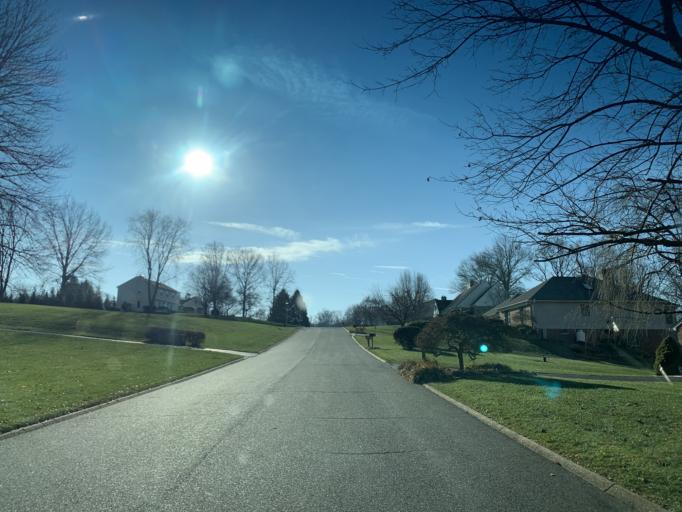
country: US
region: Maryland
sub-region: Harford County
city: South Bel Air
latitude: 39.5686
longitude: -76.2675
